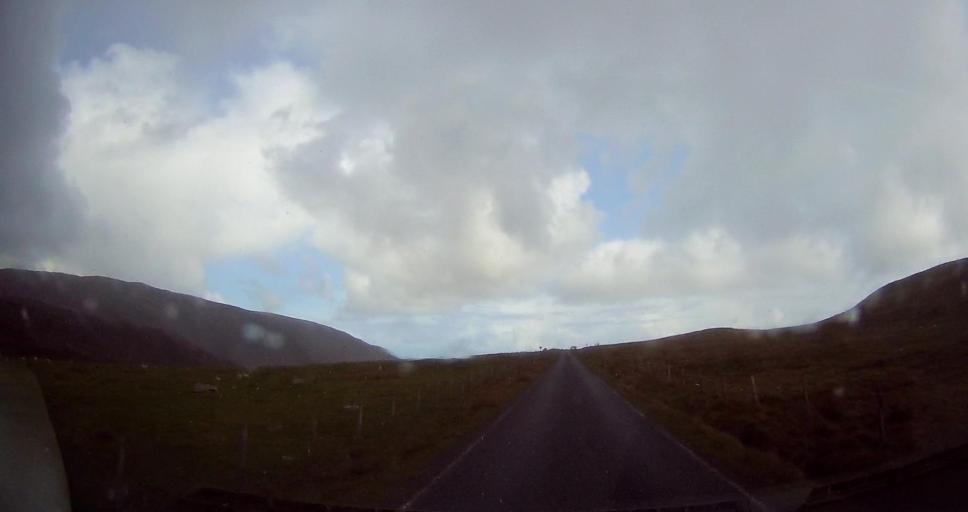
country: GB
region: Scotland
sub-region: Shetland Islands
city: Lerwick
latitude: 60.5548
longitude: -1.3400
